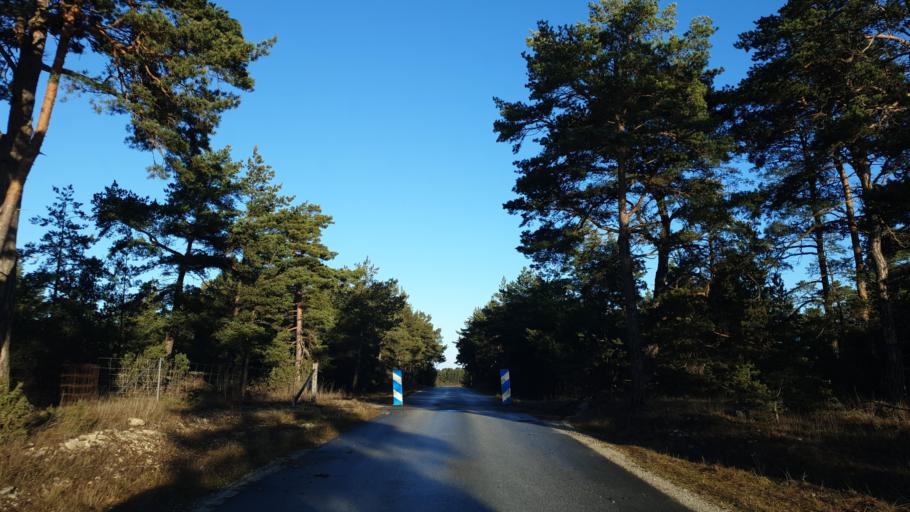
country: SE
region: Gotland
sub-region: Gotland
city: Slite
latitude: 57.9382
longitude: 19.1491
